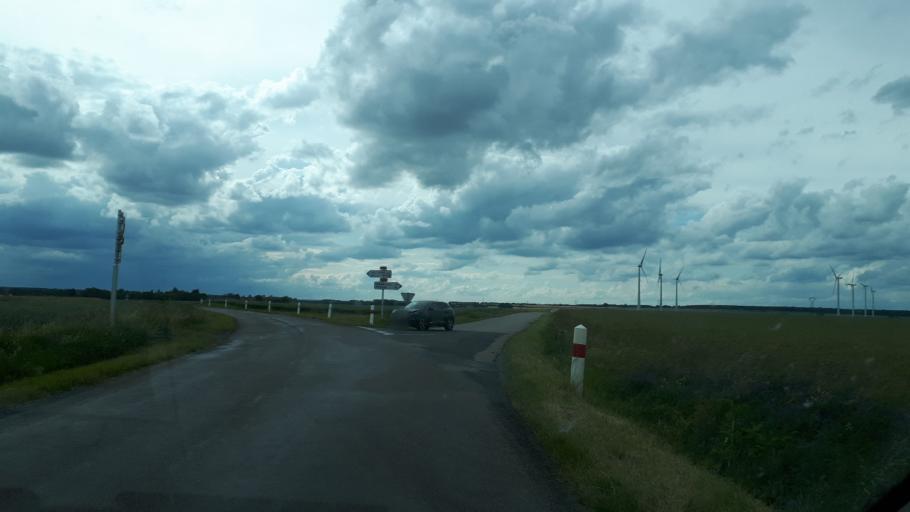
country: FR
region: Centre
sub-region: Departement du Cher
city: Massay
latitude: 47.1020
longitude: 1.9545
